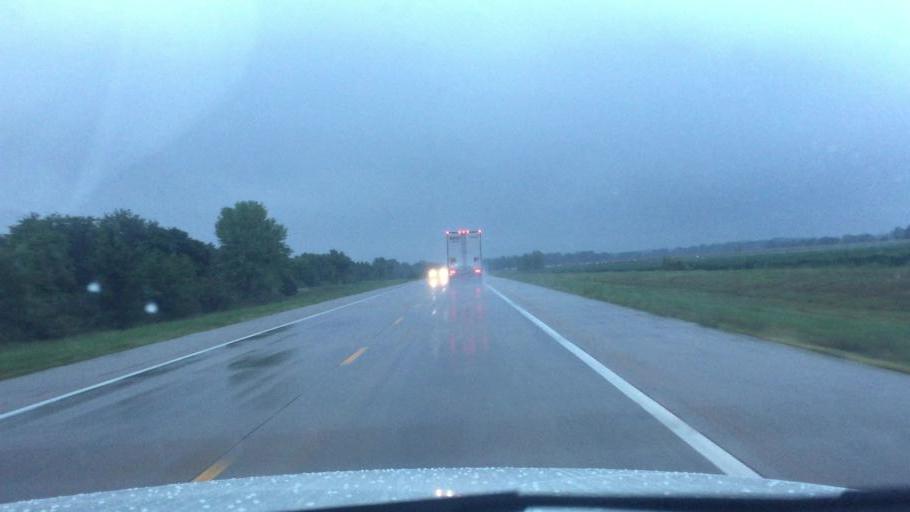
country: US
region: Kansas
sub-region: Neosho County
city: Chanute
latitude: 37.5688
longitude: -95.4709
